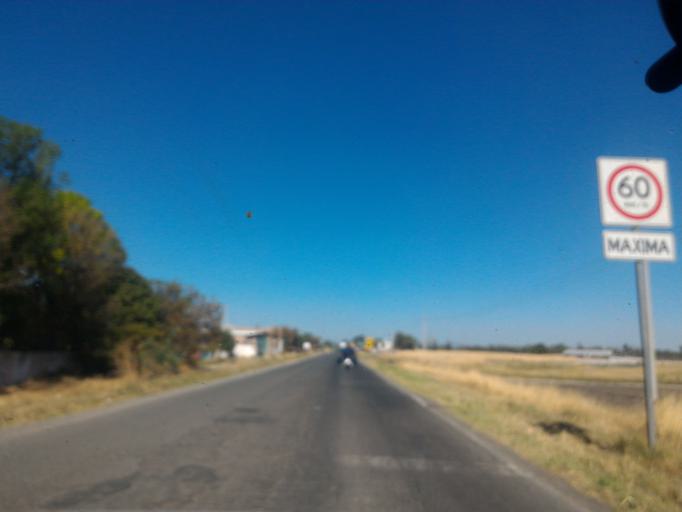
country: MX
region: Guanajuato
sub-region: San Francisco del Rincon
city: San Roque de Montes
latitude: 20.9959
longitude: -101.8152
